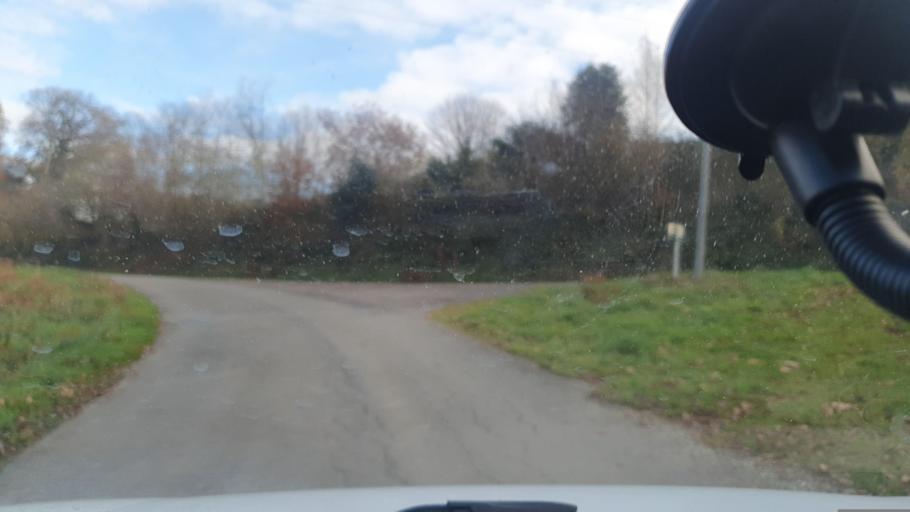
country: FR
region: Brittany
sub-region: Departement du Finistere
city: Landrevarzec
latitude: 48.1036
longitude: -4.0368
